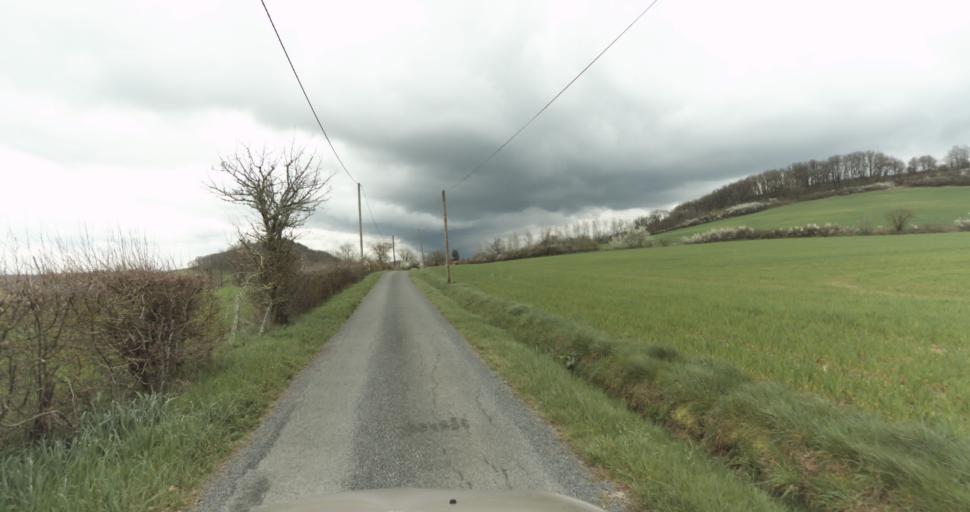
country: FR
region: Midi-Pyrenees
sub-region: Departement du Tarn
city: Frejairolles
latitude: 43.8708
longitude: 2.2071
